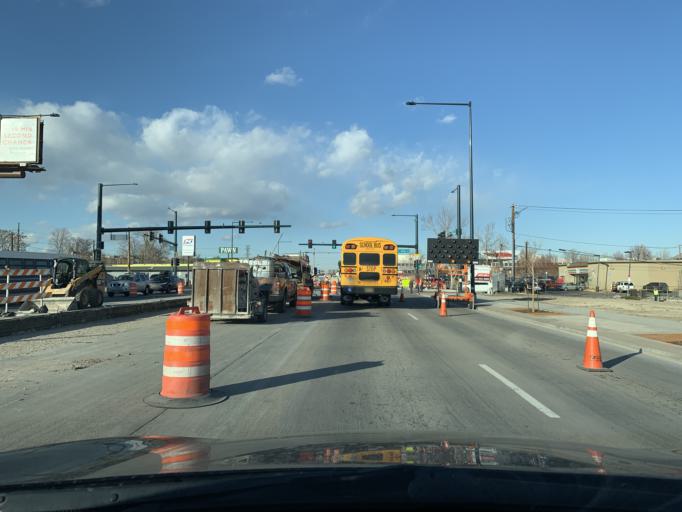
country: US
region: Colorado
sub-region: Denver County
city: Denver
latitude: 39.7324
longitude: -105.0251
